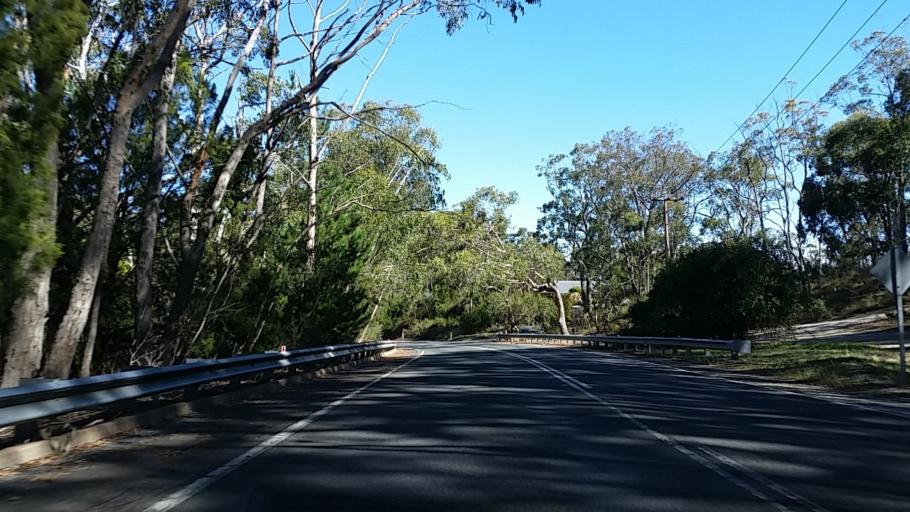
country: AU
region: South Australia
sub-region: Adelaide Hills
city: Crafers
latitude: -34.9887
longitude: 138.7081
